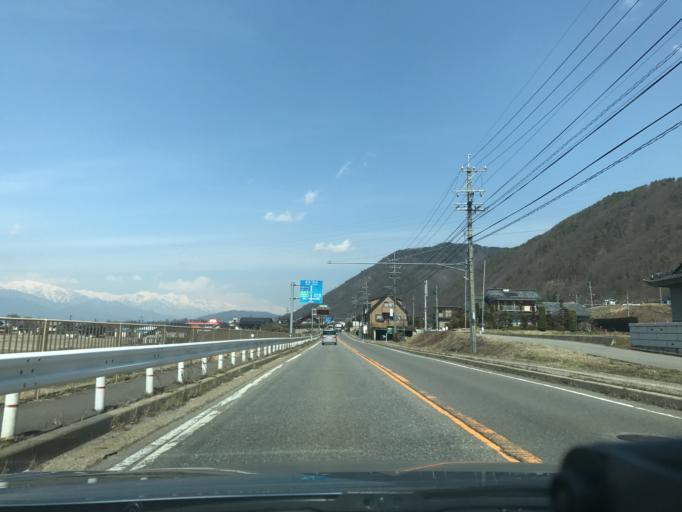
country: JP
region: Nagano
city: Toyoshina
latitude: 36.2974
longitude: 137.9411
